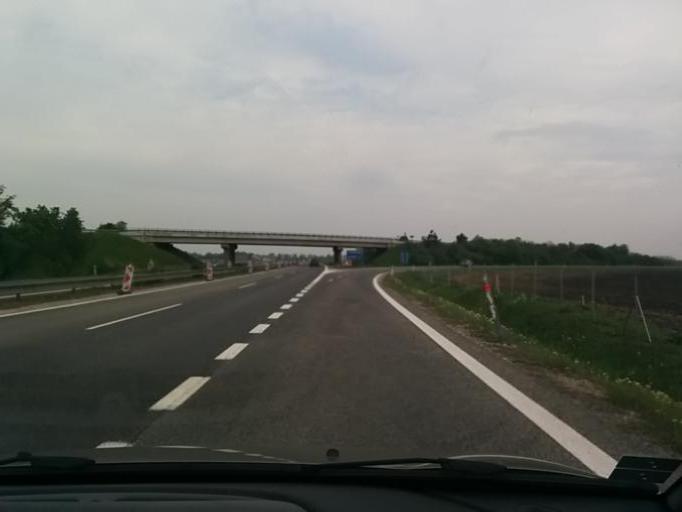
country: SK
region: Trnavsky
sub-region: Okres Galanta
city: Galanta
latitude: 48.2721
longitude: 17.7181
